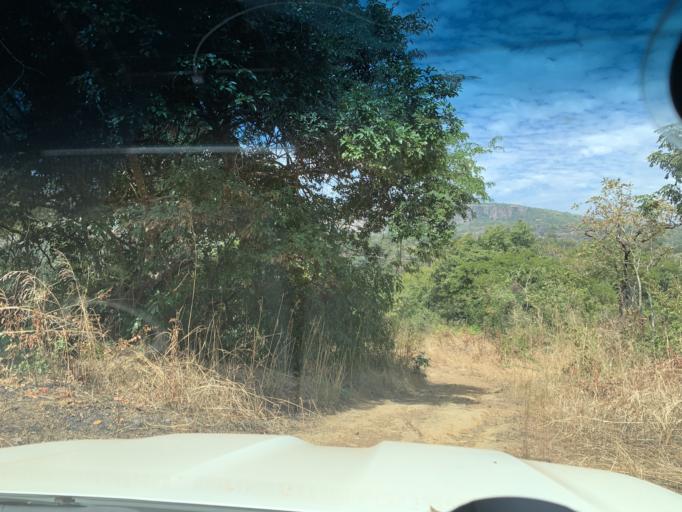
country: GN
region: Mamou
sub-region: Pita
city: Pita
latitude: 10.9947
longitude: -12.4891
